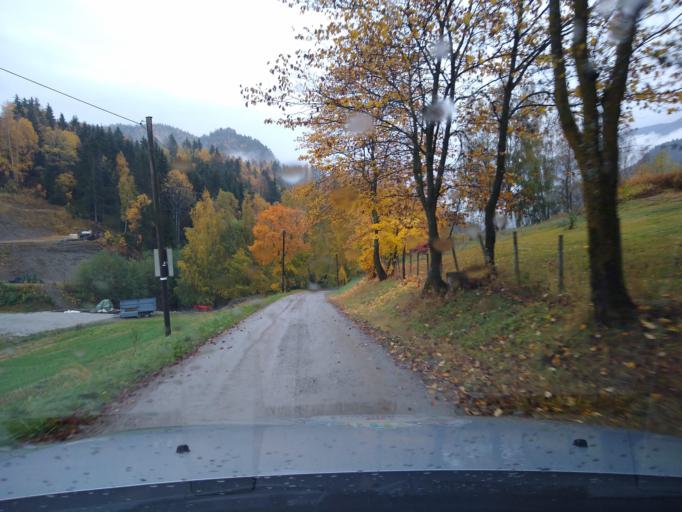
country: NO
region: Oppland
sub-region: Ringebu
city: Ringebu
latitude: 61.5044
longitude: 10.1723
